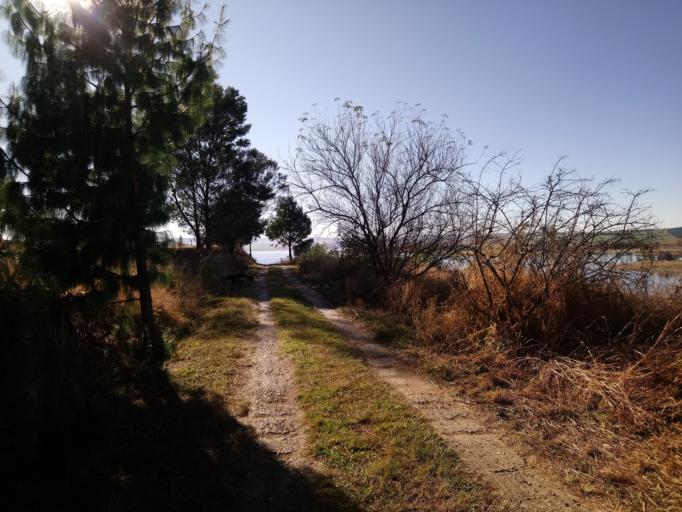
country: ZA
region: KwaZulu-Natal
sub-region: uMgungundlovu District Municipality
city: Mooirivier
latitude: -29.3348
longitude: 29.9201
